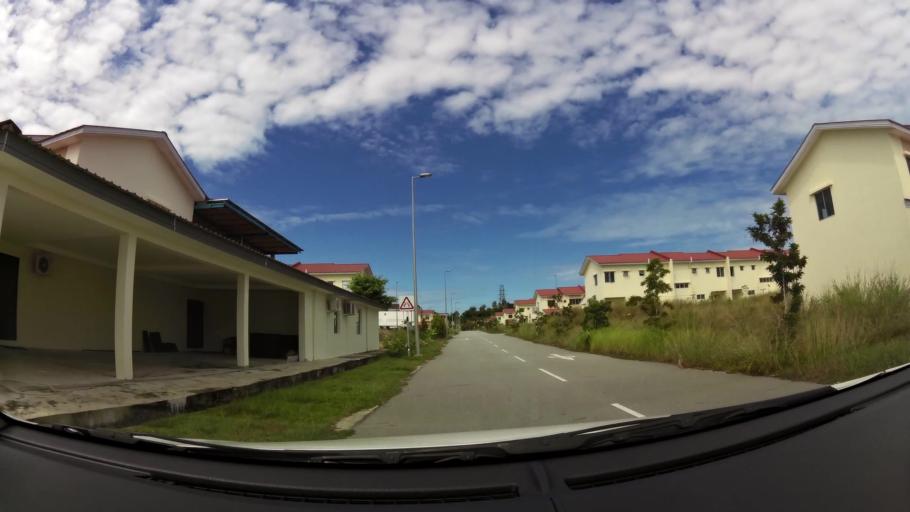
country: BN
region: Brunei and Muara
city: Bandar Seri Begawan
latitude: 4.9738
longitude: 115.0052
